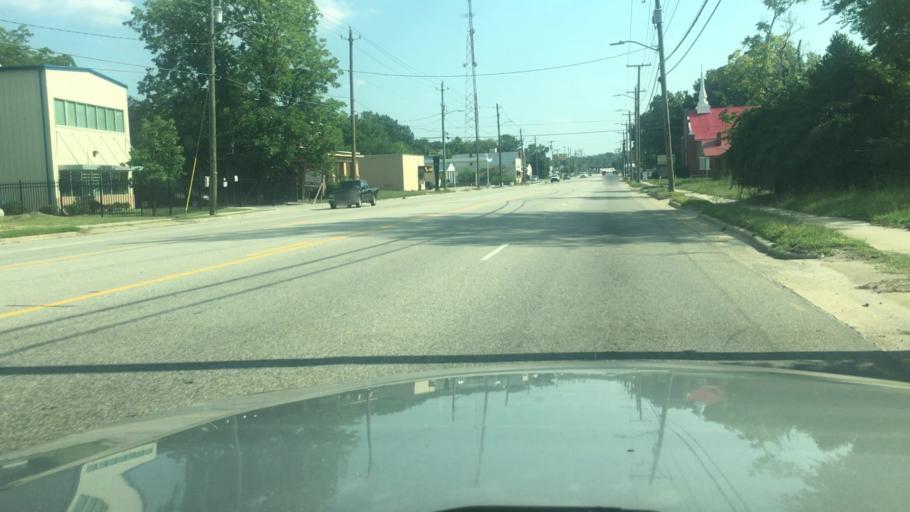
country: US
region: North Carolina
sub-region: Cumberland County
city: Fayetteville
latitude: 35.0456
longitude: -78.8808
